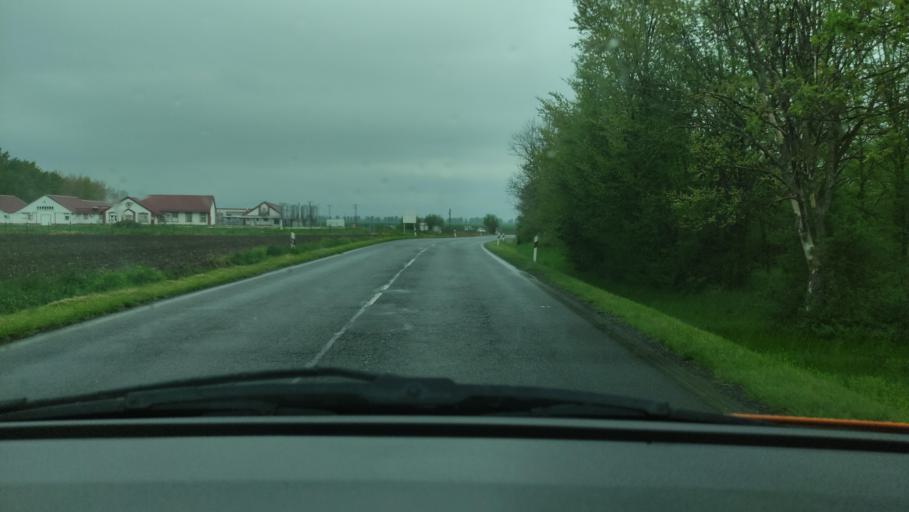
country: HU
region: Baranya
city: Mohacs
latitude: 45.9270
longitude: 18.6596
